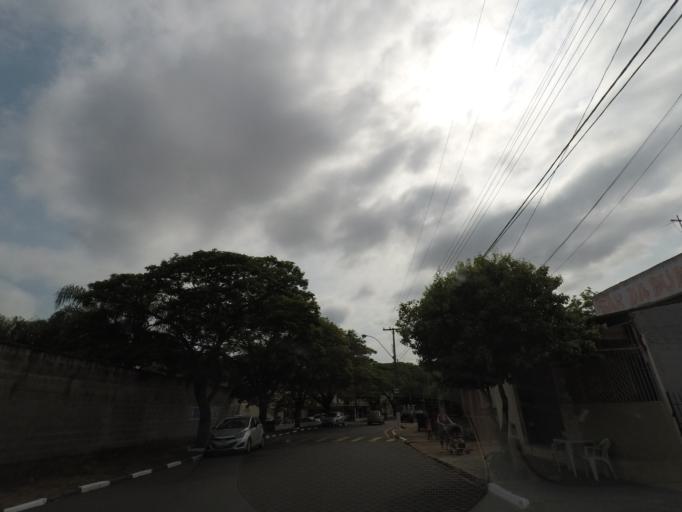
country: BR
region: Sao Paulo
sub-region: Paulinia
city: Paulinia
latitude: -22.7635
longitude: -47.1568
